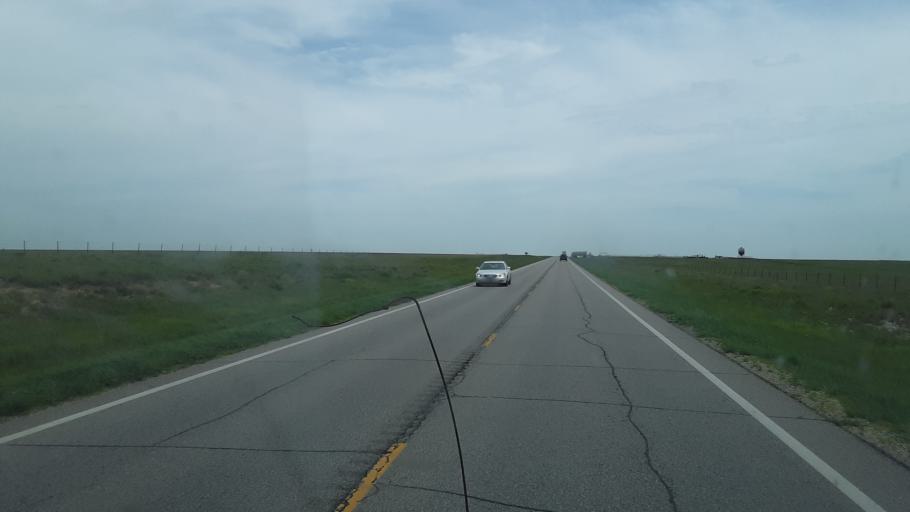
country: US
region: Kansas
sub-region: Greenwood County
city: Eureka
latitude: 37.8102
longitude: -96.5677
